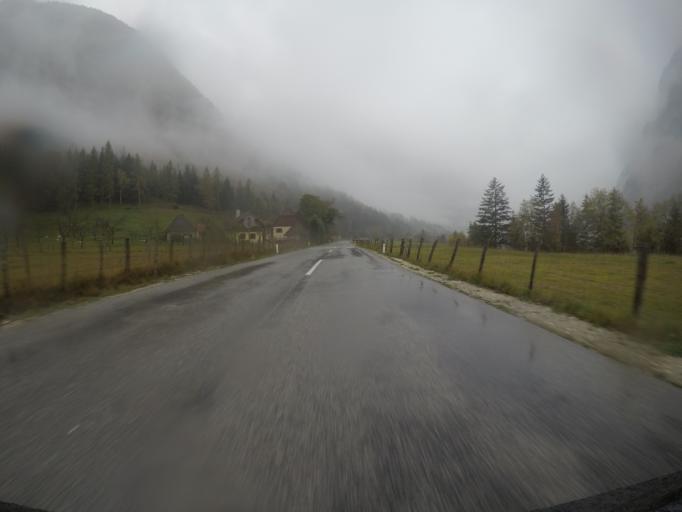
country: SI
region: Kranjska Gora
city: Kranjska Gora
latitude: 46.3796
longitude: 13.7510
